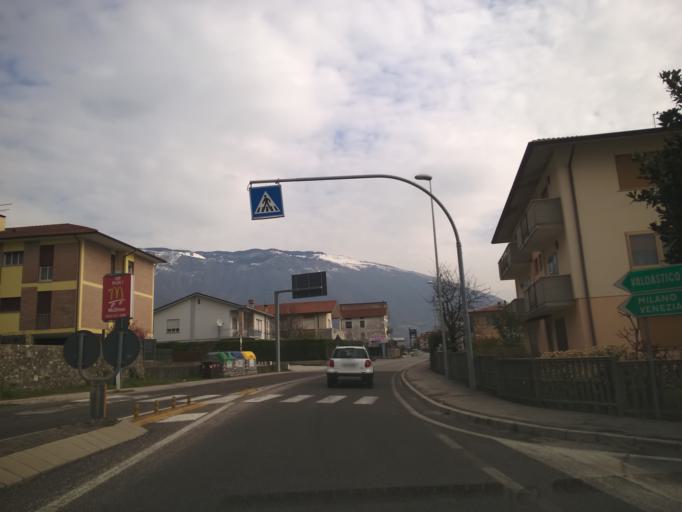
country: IT
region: Veneto
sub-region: Provincia di Vicenza
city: Piovene Rocchette
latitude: 45.7532
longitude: 11.4308
